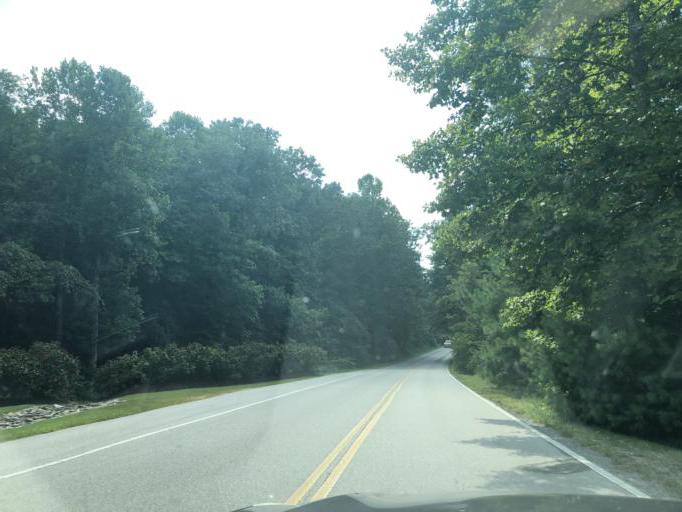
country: US
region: Tennessee
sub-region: Franklin County
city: Sewanee
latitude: 35.2079
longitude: -85.9024
